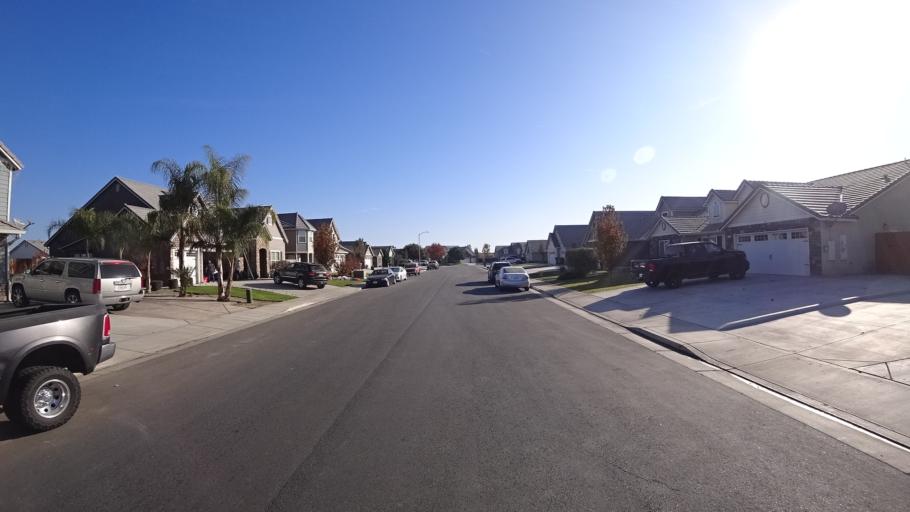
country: US
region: California
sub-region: Kern County
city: Greenfield
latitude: 35.2730
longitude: -119.0676
